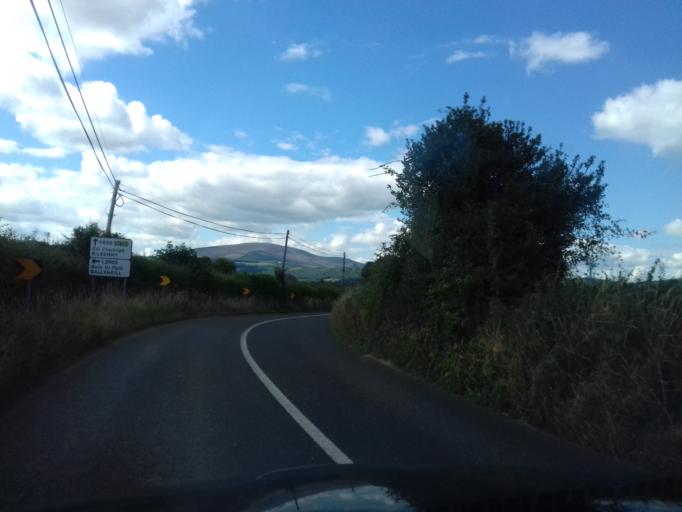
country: IE
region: Munster
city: Carrick-on-Suir
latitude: 52.3685
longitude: -7.4451
